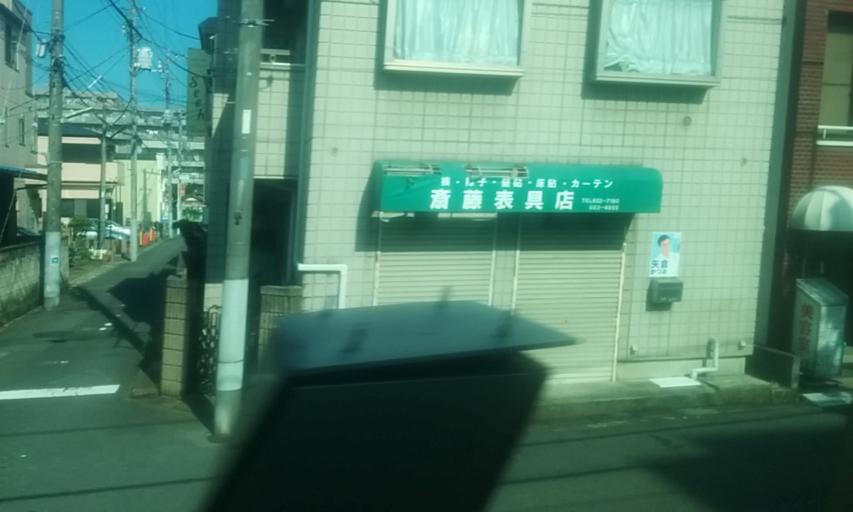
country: JP
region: Saitama
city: Hasuda
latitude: 35.9502
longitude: 139.6407
